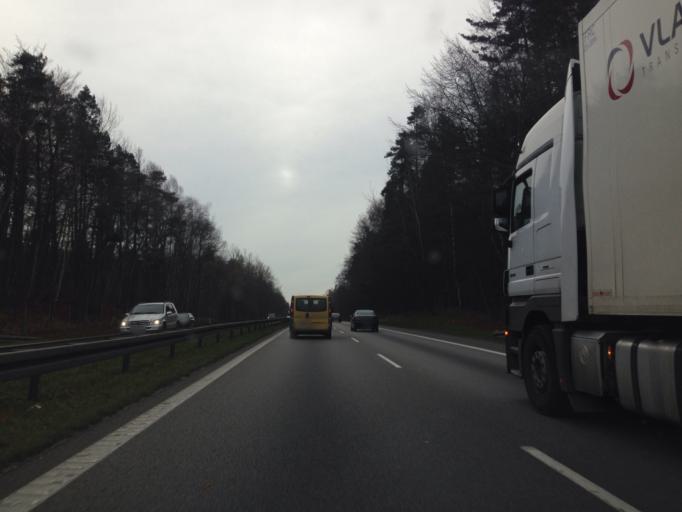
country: PL
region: Pomeranian Voivodeship
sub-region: Gdynia
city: Wielki Kack
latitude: 54.4435
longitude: 18.4904
